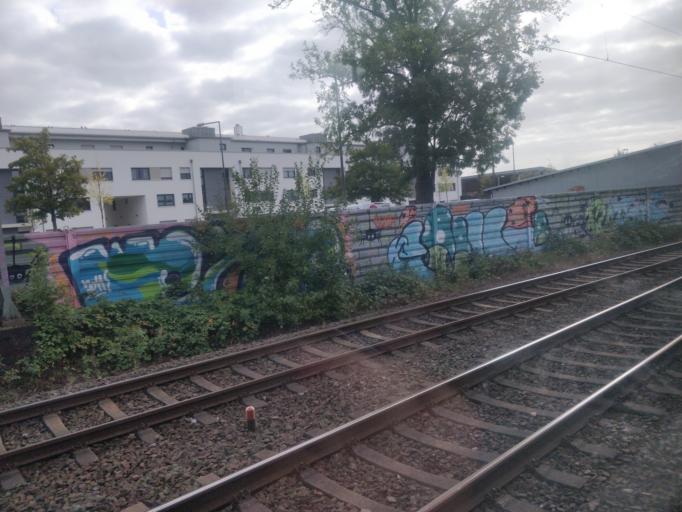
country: DE
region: North Rhine-Westphalia
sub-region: Regierungsbezirk Koln
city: Wahn-Heide
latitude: 50.8572
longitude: 7.0798
